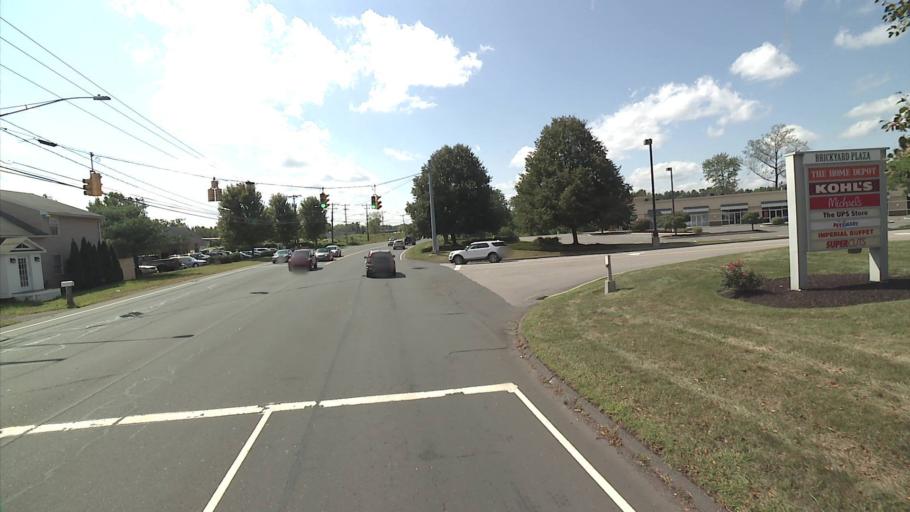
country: US
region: Connecticut
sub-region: Hartford County
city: Kensington
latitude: 41.6420
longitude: -72.7294
